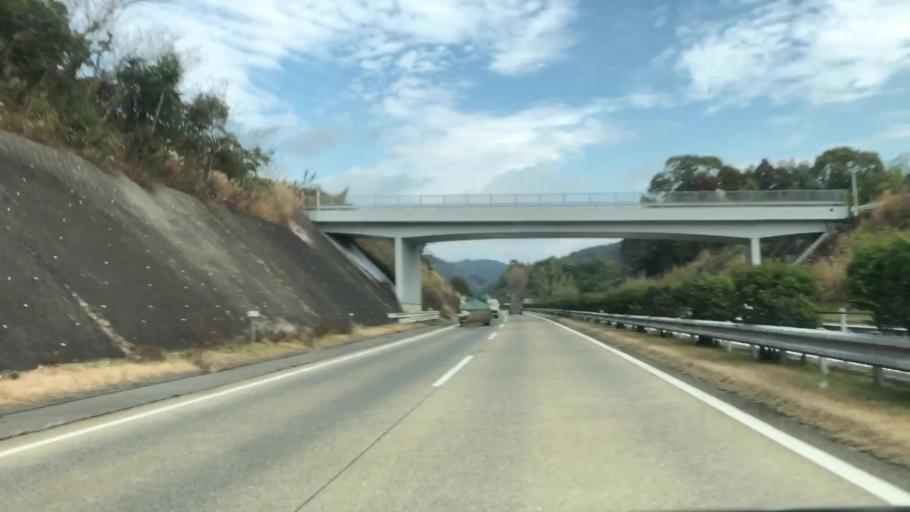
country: JP
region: Saga Prefecture
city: Kanzakimachi-kanzaki
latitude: 33.3315
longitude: 130.3197
